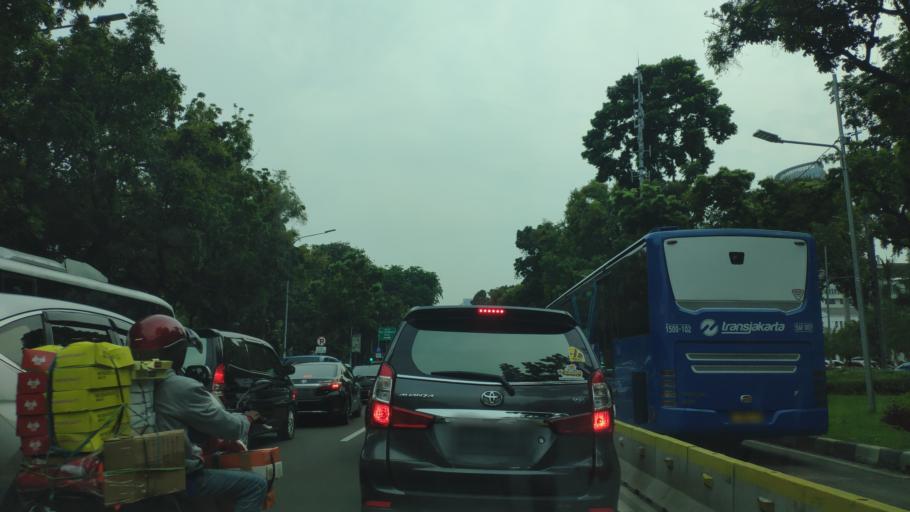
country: ID
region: Jakarta Raya
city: Jakarta
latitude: -6.1751
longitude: 106.8230
